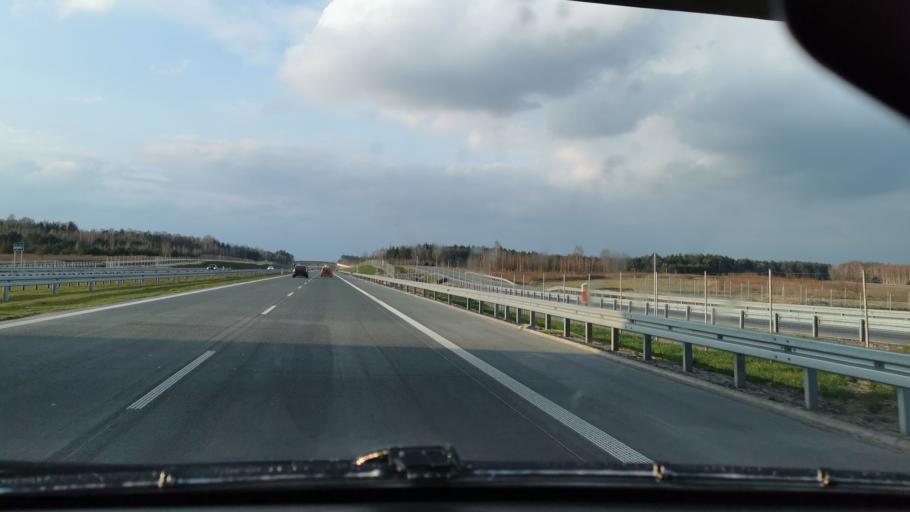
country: PL
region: Masovian Voivodeship
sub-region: Powiat garwolinski
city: Pilawa
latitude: 51.9749
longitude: 21.5593
